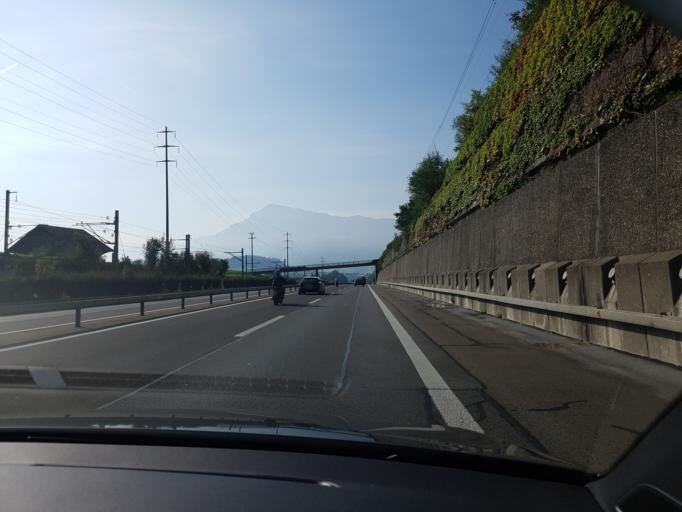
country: CH
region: Lucerne
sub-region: Lucerne-Land District
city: Meierskappel
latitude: 47.1329
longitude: 8.4493
